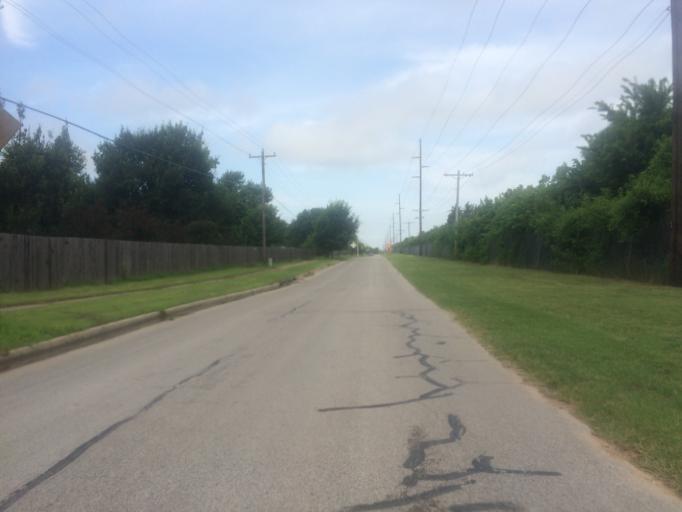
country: US
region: Oklahoma
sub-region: Cleveland County
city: Noble
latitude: 35.1751
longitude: -97.4263
